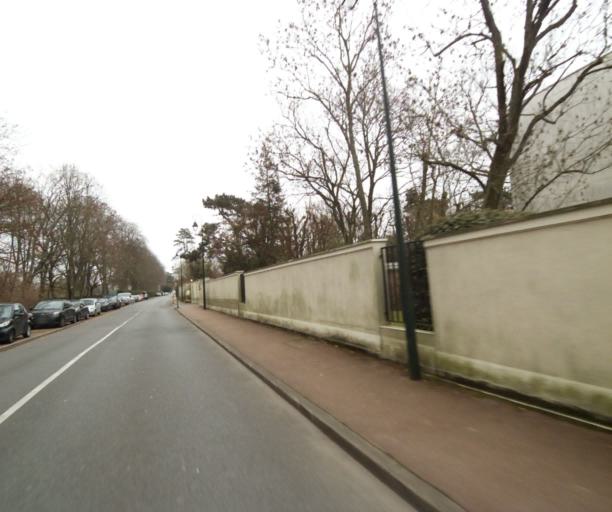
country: FR
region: Ile-de-France
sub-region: Departement des Hauts-de-Seine
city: Garches
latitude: 48.8484
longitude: 2.1730
